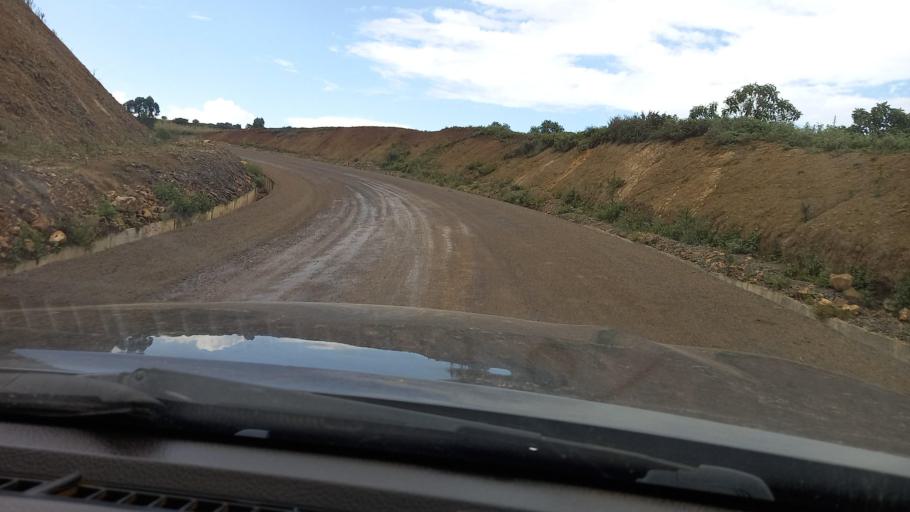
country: ET
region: Southern Nations, Nationalities, and People's Region
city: Mizan Teferi
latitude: 6.2168
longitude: 35.6370
